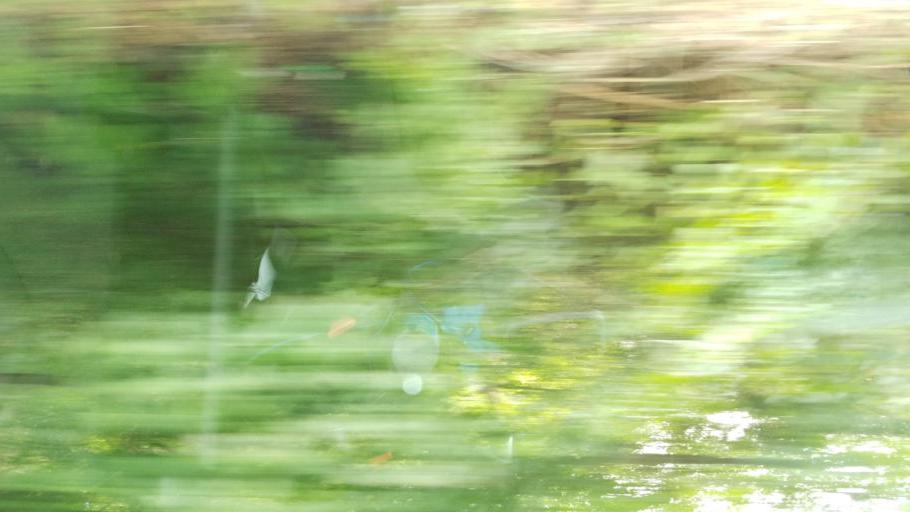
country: US
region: Ohio
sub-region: Mahoning County
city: Boardman
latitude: 41.0389
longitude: -80.6506
